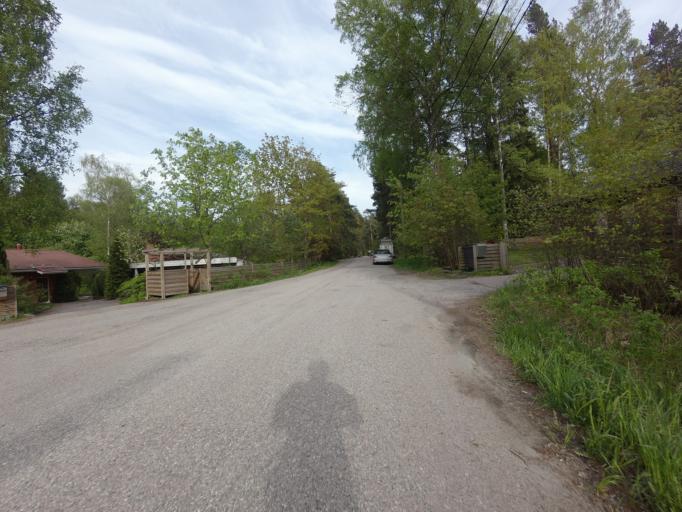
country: FI
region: Uusimaa
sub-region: Helsinki
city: Koukkuniemi
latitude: 60.1456
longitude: 24.6929
